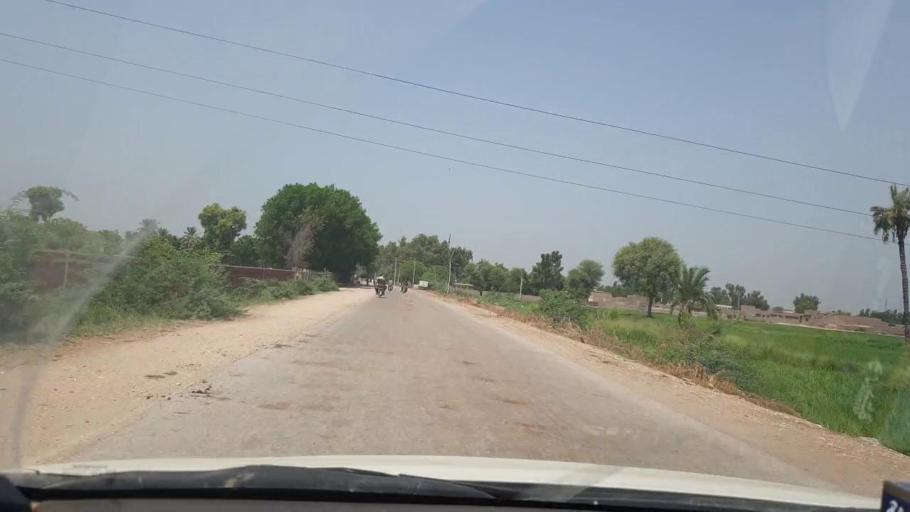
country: PK
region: Sindh
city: Shikarpur
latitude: 27.9543
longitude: 68.6571
